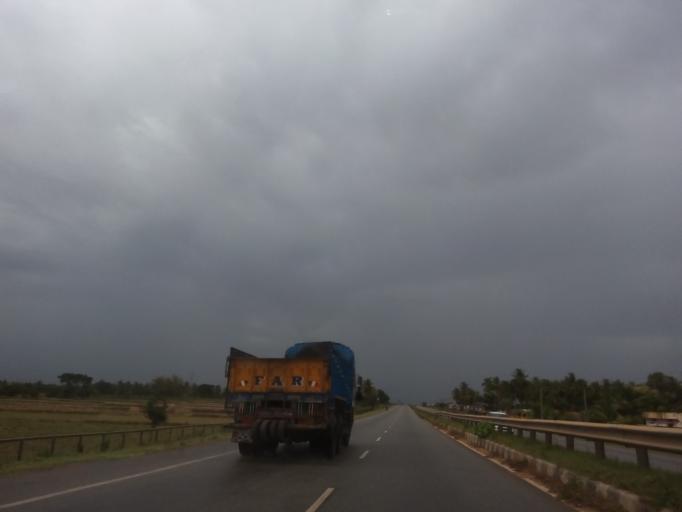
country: IN
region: Karnataka
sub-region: Davanagere
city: Harihar
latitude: 14.4487
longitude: 75.8820
